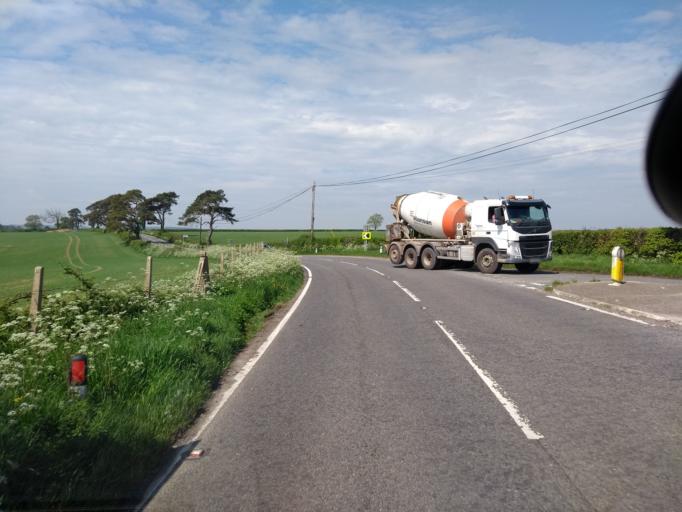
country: GB
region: England
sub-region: Somerset
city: Chard
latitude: 50.8849
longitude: -3.0100
